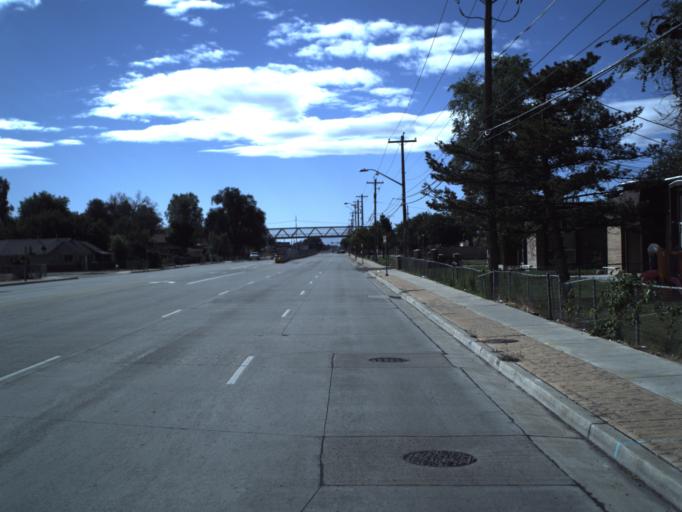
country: US
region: Utah
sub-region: Salt Lake County
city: Centerfield
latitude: 40.7160
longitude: -111.9391
